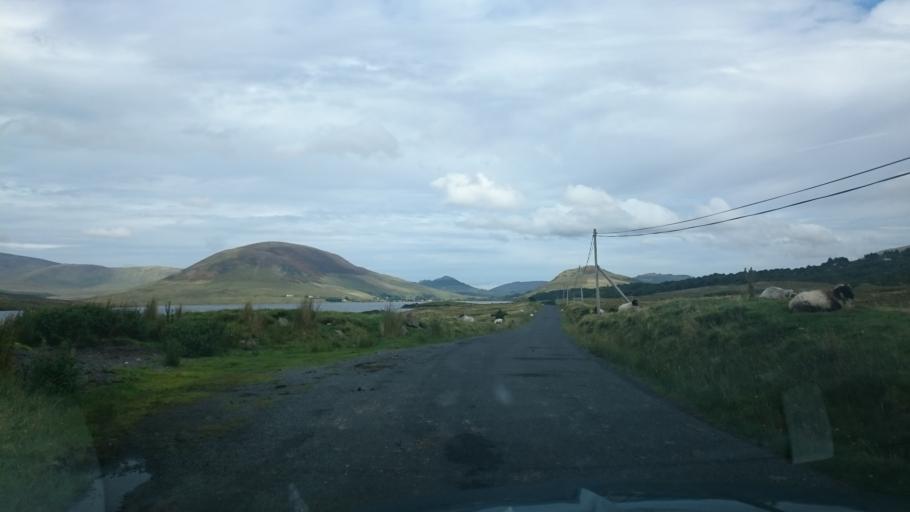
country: IE
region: Connaught
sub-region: Maigh Eo
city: Westport
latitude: 53.9357
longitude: -9.5681
